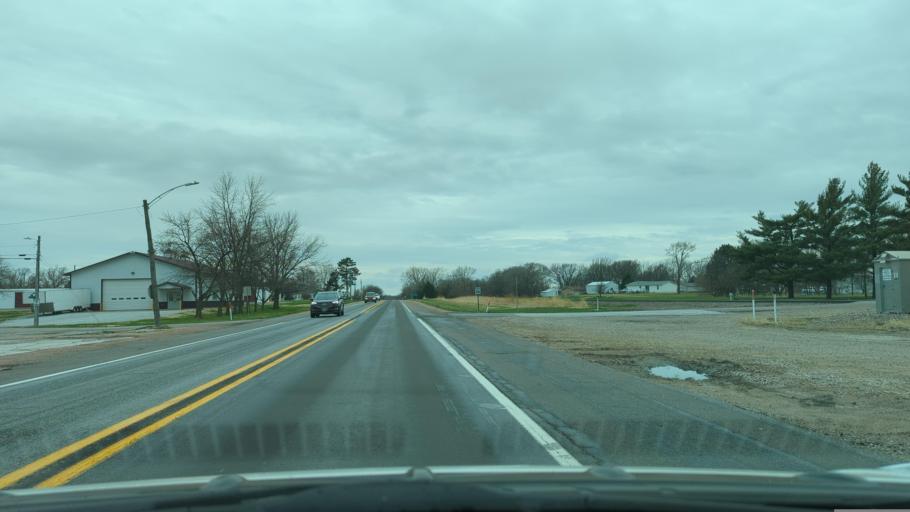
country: US
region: Nebraska
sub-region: Lancaster County
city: Waverly
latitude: 40.9607
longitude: -96.4432
